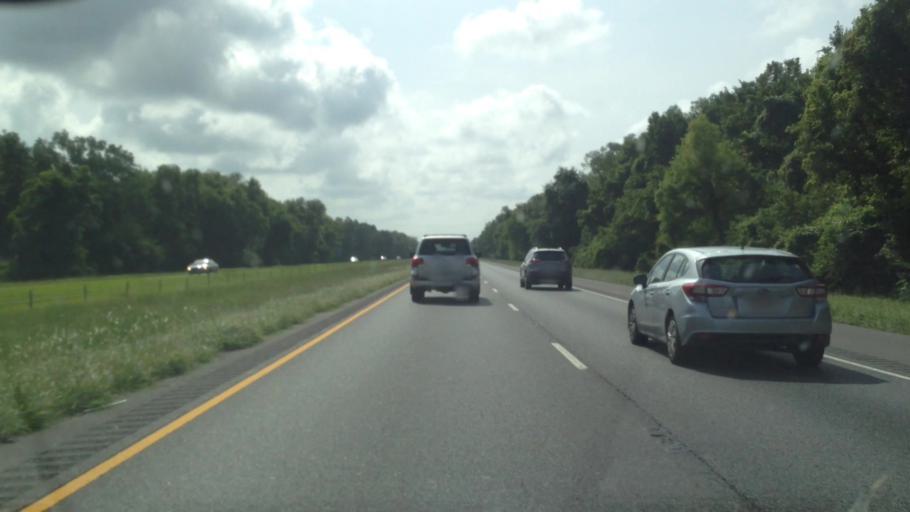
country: US
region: Louisiana
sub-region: Ascension Parish
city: Sorrento
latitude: 30.1657
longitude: -90.8560
